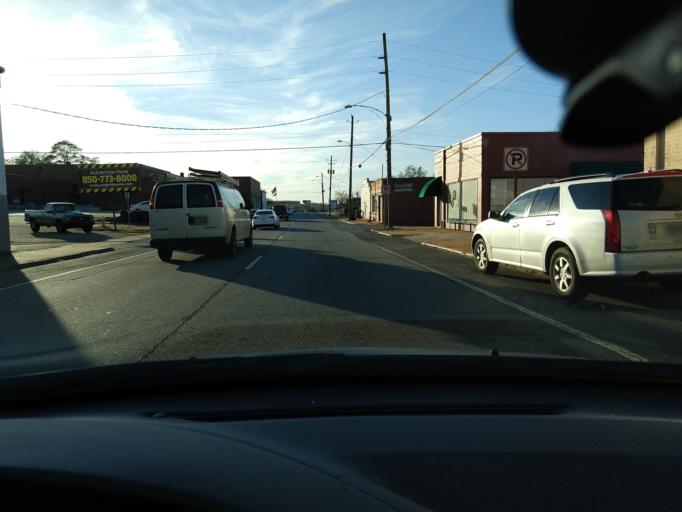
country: US
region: Georgia
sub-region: Sumter County
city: Americus
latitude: 32.0733
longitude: -84.2374
